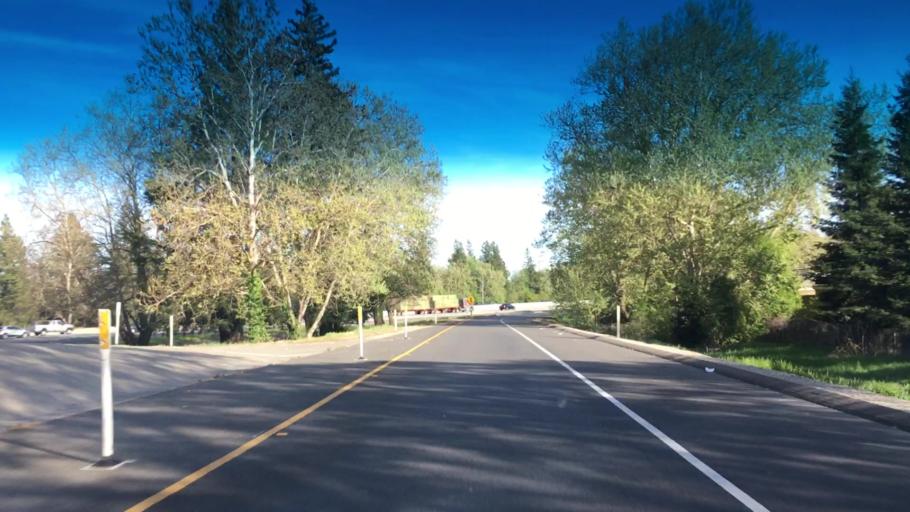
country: US
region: California
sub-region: Sacramento County
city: Parkway
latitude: 38.4946
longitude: -121.5177
